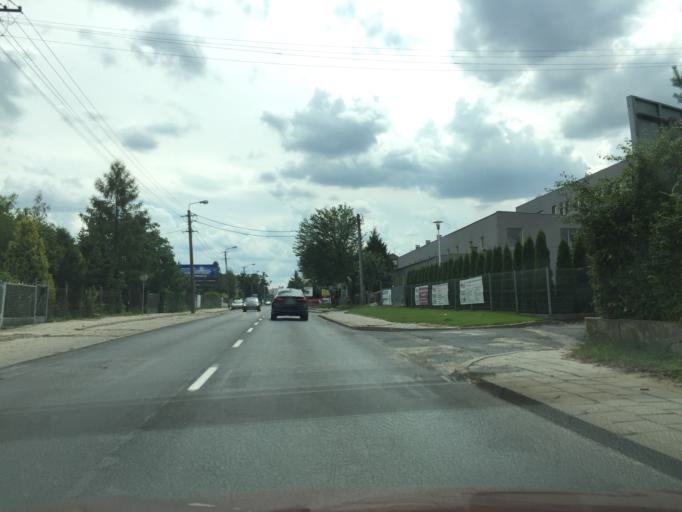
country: PL
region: Greater Poland Voivodeship
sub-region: Kalisz
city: Kalisz
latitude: 51.7475
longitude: 18.0965
